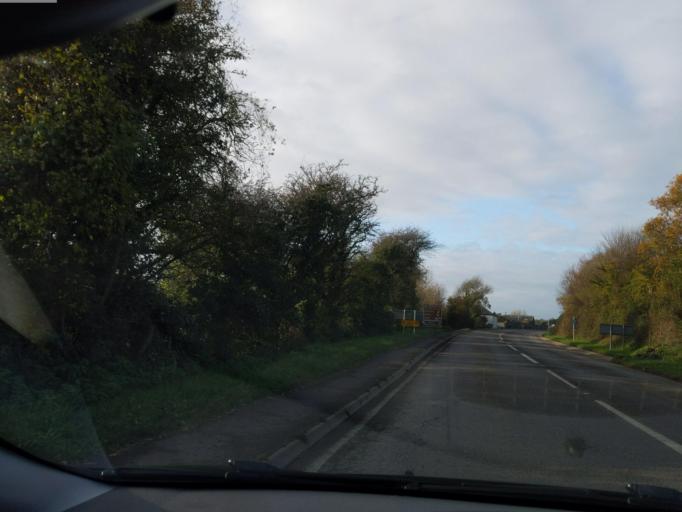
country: GB
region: England
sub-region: Cornwall
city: Wadebridge
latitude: 50.5097
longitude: -4.8124
